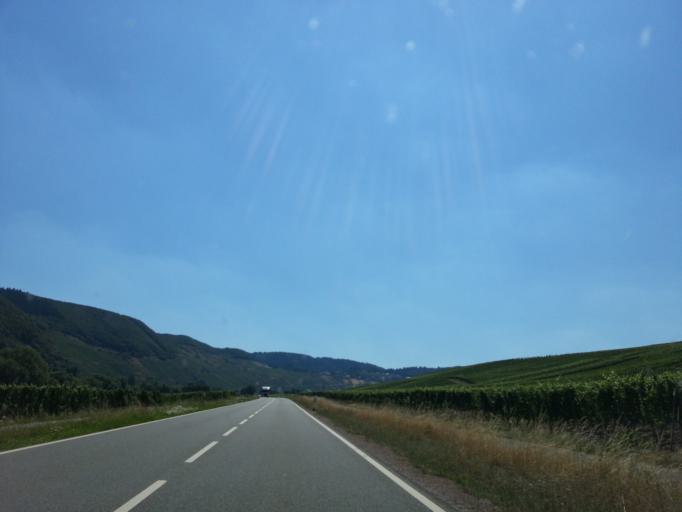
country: DE
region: Rheinland-Pfalz
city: Kowerich
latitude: 49.8378
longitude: 6.8940
